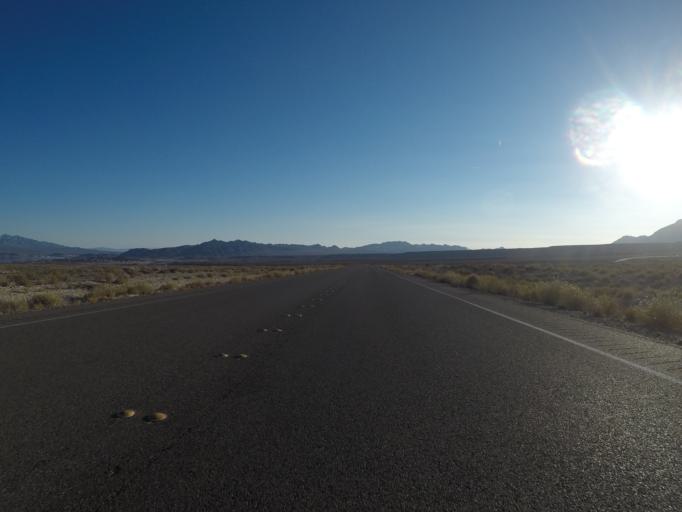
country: US
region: Nevada
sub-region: Clark County
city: Moapa Valley
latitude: 36.3732
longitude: -114.4432
